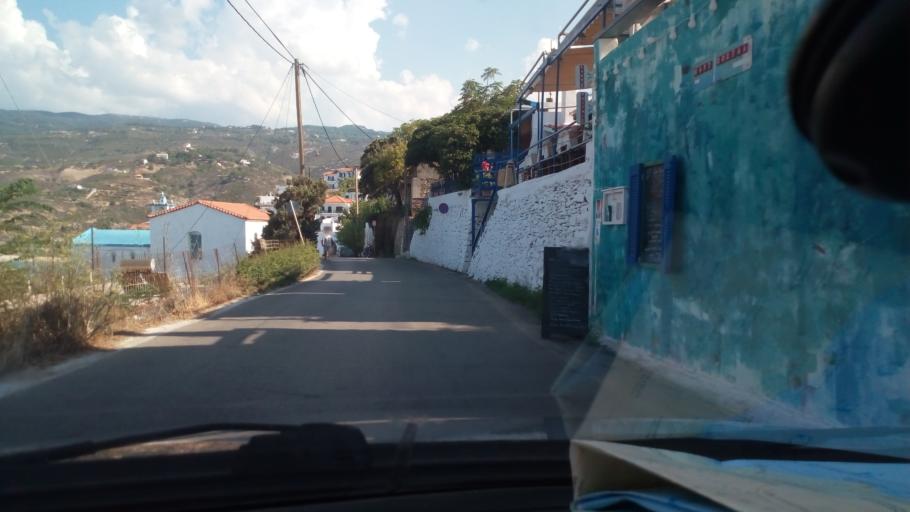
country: GR
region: North Aegean
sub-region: Nomos Samou
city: Agios Kirykos
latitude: 37.6348
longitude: 26.0875
